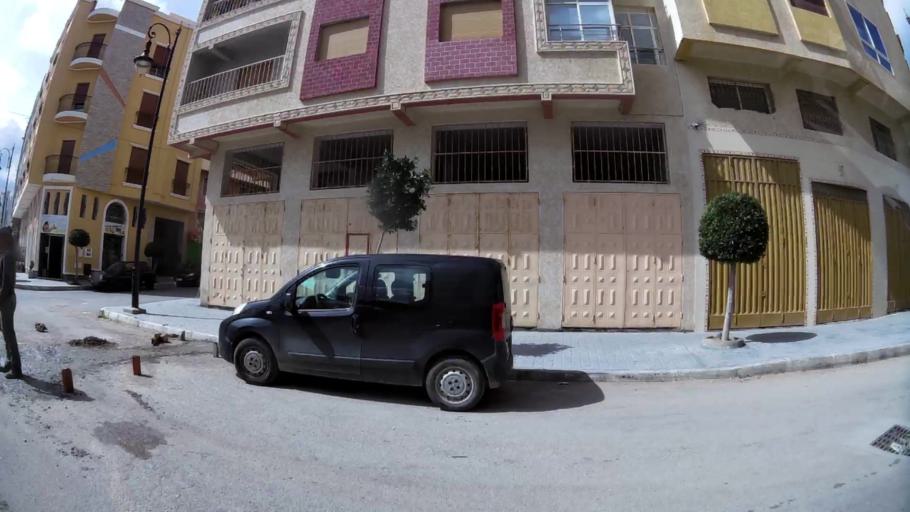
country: MA
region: Tanger-Tetouan
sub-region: Tanger-Assilah
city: Tangier
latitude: 35.7686
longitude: -5.7617
